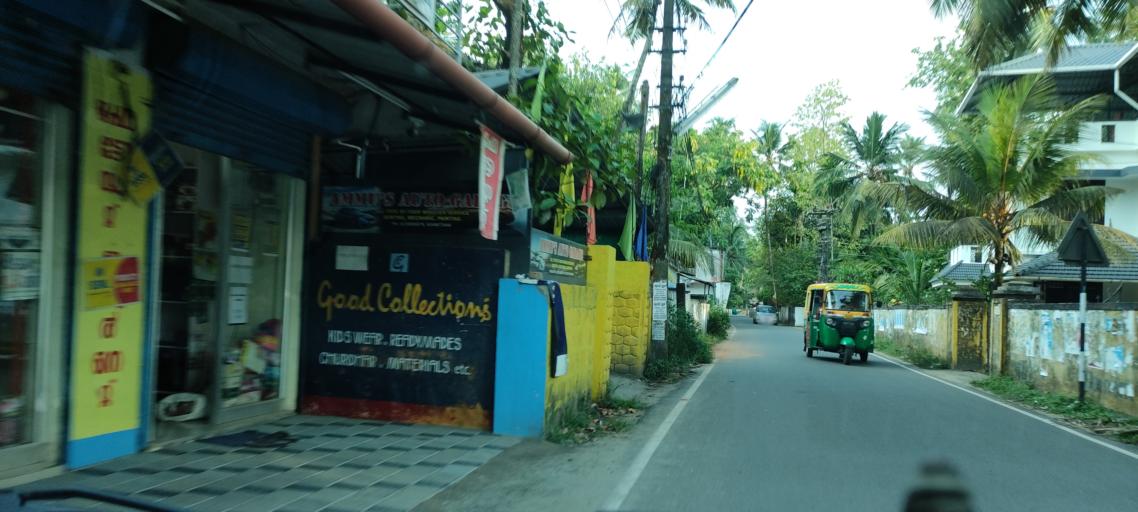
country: IN
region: Kerala
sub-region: Alappuzha
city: Arukutti
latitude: 9.8968
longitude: 76.3089
